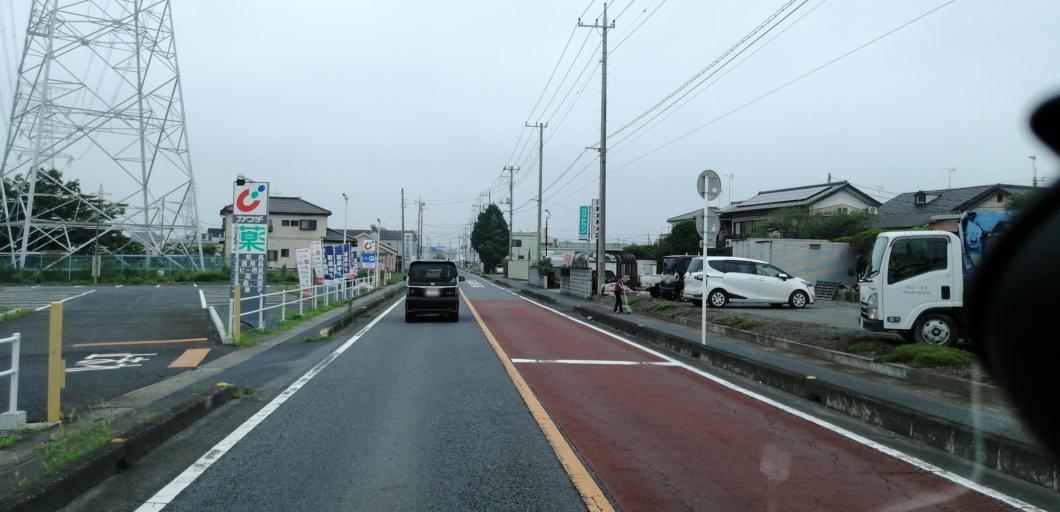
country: JP
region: Saitama
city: Kukichuo
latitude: 36.1036
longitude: 139.6606
